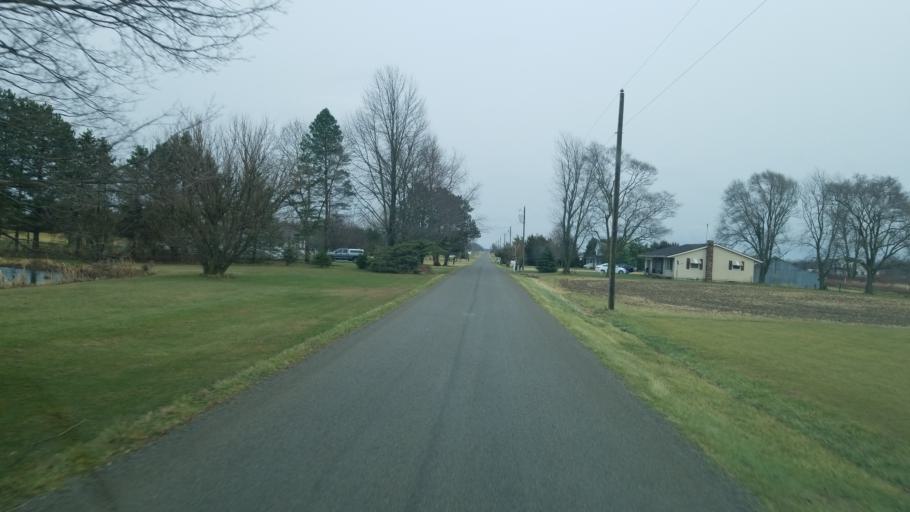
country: US
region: Ohio
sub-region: Union County
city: Marysville
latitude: 40.3321
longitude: -83.3729
